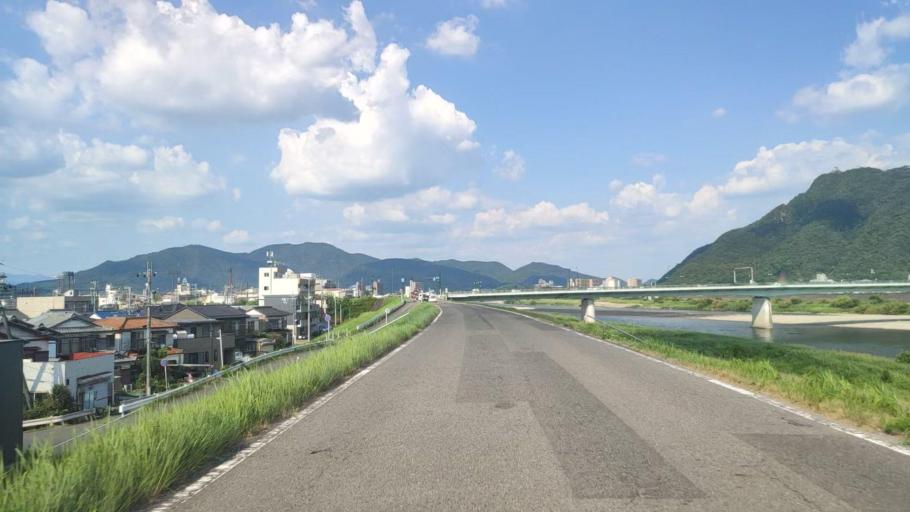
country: JP
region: Gifu
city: Gifu-shi
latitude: 35.4333
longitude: 136.7592
